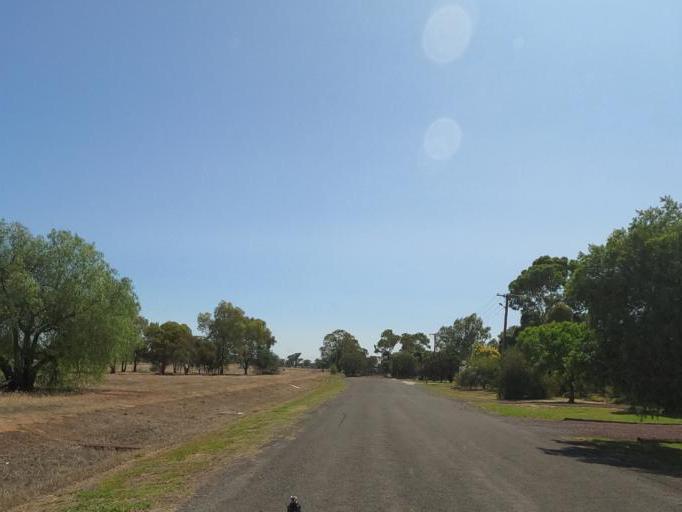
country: AU
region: New South Wales
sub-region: Corowa Shire
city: Mulwala
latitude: -35.9847
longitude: 146.0022
